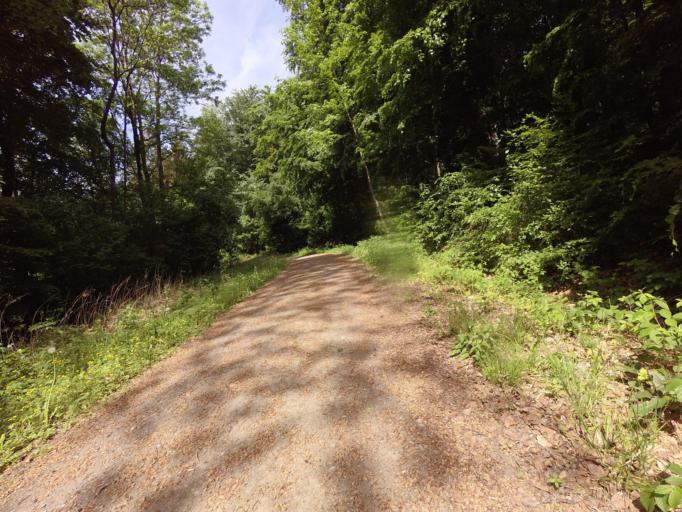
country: DE
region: Lower Saxony
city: Evessen
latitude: 52.1966
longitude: 10.7370
